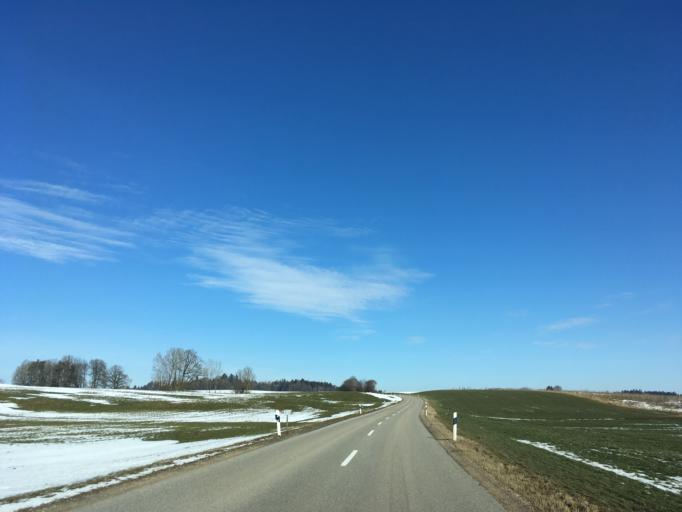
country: DE
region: Bavaria
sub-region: Upper Bavaria
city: Rechtmehring
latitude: 48.0979
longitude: 12.1592
